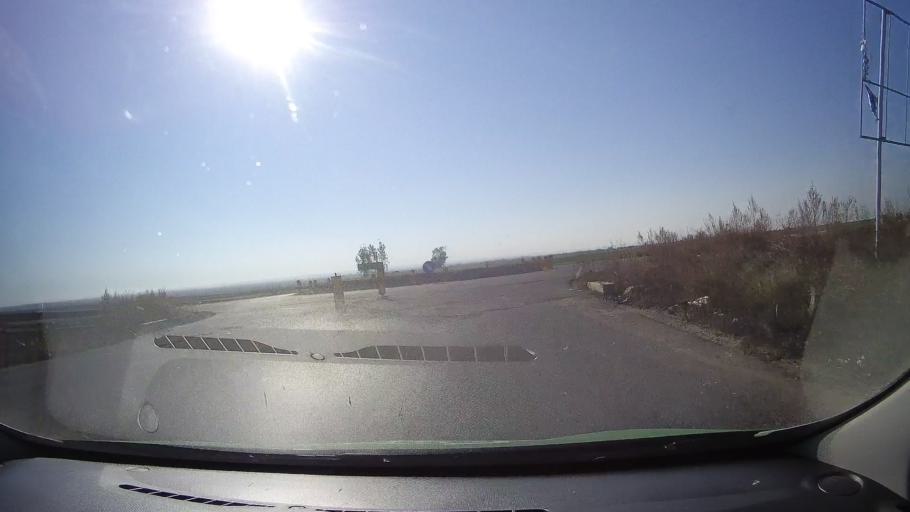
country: RO
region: Satu Mare
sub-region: Comuna Tiream
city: Tiream
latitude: 47.6433
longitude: 22.4643
